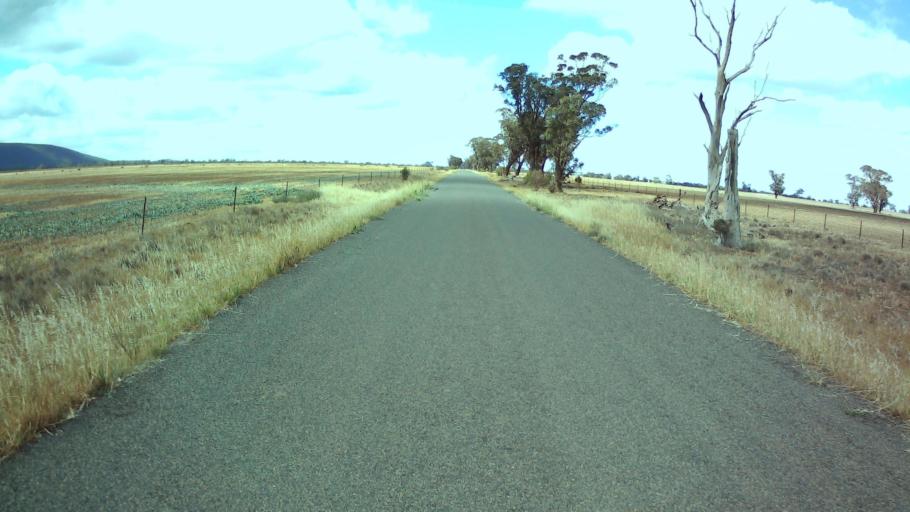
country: AU
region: New South Wales
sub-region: Weddin
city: Grenfell
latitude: -33.8714
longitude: 147.9264
